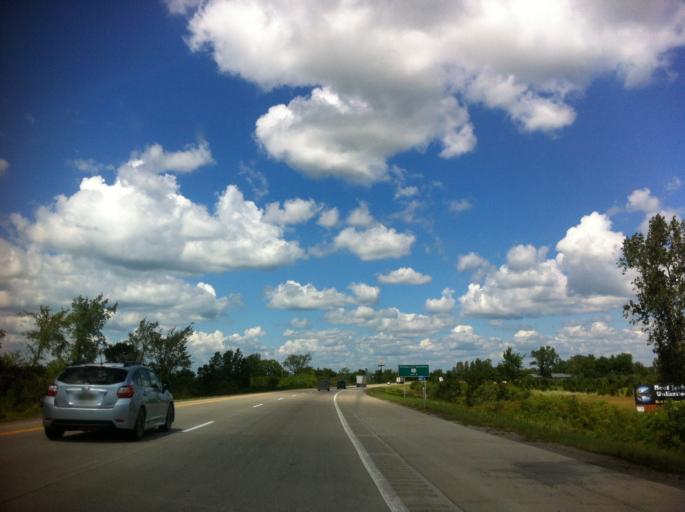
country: US
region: Ohio
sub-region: Lucas County
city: Sylvania
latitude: 41.7862
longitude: -83.6957
